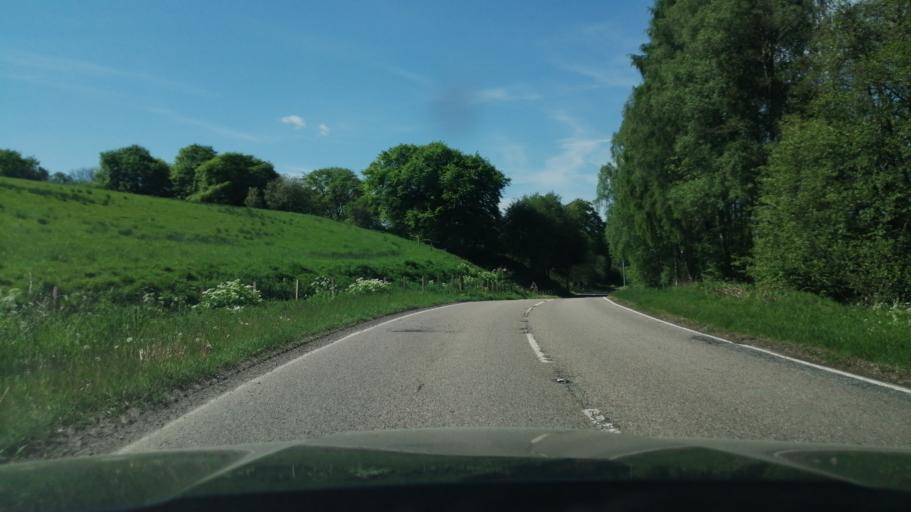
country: GB
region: Scotland
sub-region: Moray
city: Dufftown
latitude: 57.5034
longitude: -3.1300
